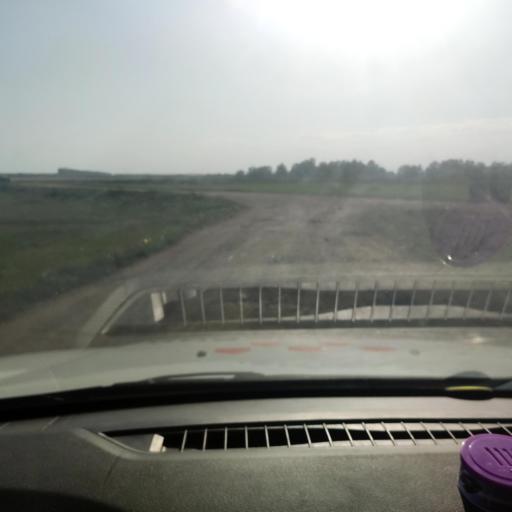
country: RU
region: Bashkortostan
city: Asanovo
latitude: 54.9957
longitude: 55.5736
